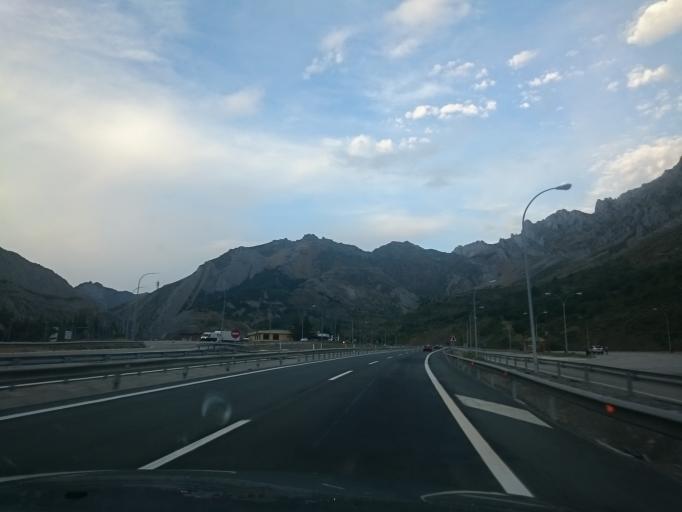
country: ES
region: Castille and Leon
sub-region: Provincia de Leon
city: Sena de Luna
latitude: 42.9282
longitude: -5.8594
